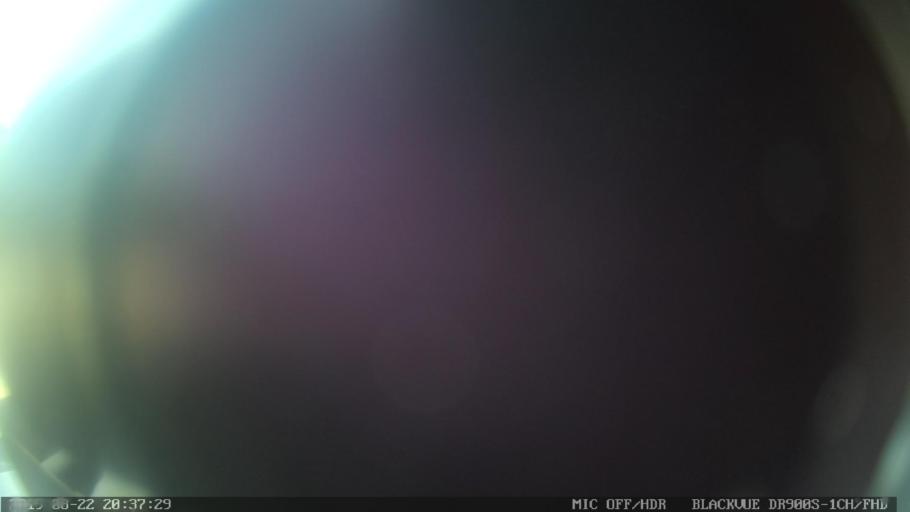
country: PT
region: Portalegre
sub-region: Nisa
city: Nisa
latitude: 39.6746
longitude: -7.7347
